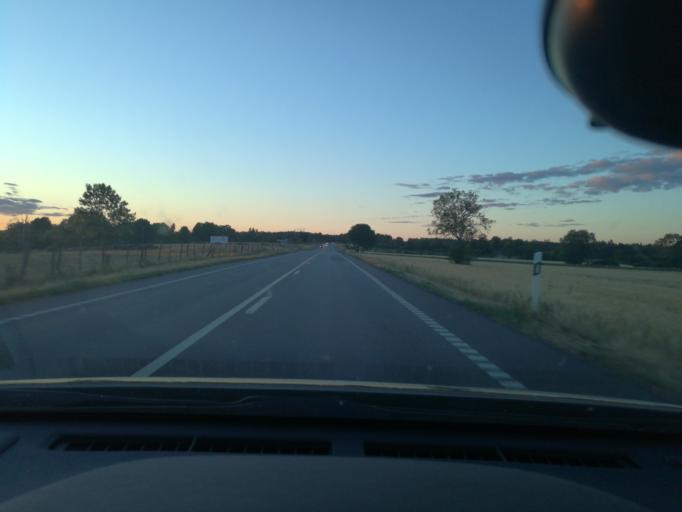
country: SE
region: Kalmar
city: Faerjestaden
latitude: 56.7381
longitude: 16.5455
